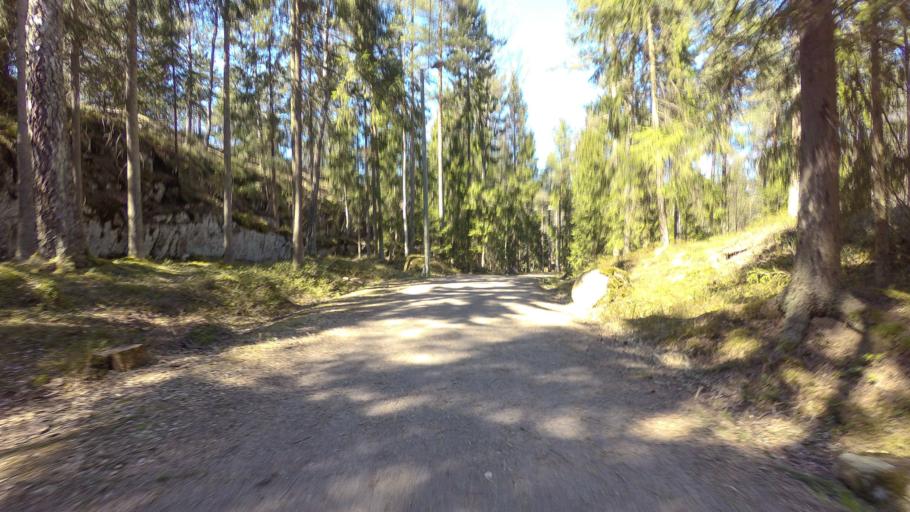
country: FI
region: Uusimaa
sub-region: Helsinki
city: Vantaa
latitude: 60.2264
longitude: 25.1387
